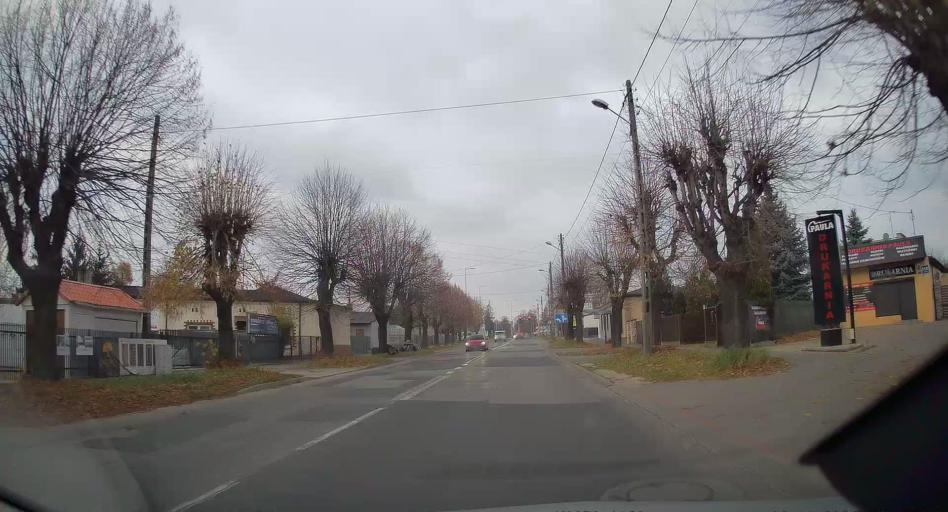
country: PL
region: Silesian Voivodeship
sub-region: Czestochowa
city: Czestochowa
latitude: 50.8212
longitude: 19.0840
